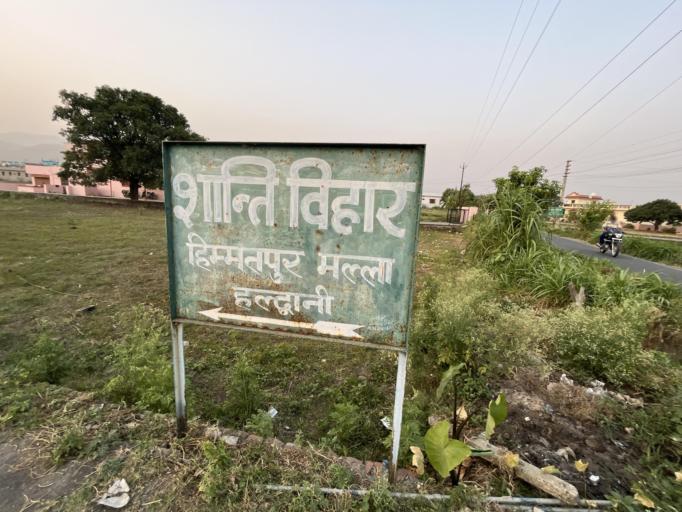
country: IN
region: Uttarakhand
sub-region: Naini Tal
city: Haldwani
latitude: 29.2202
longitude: 79.4874
